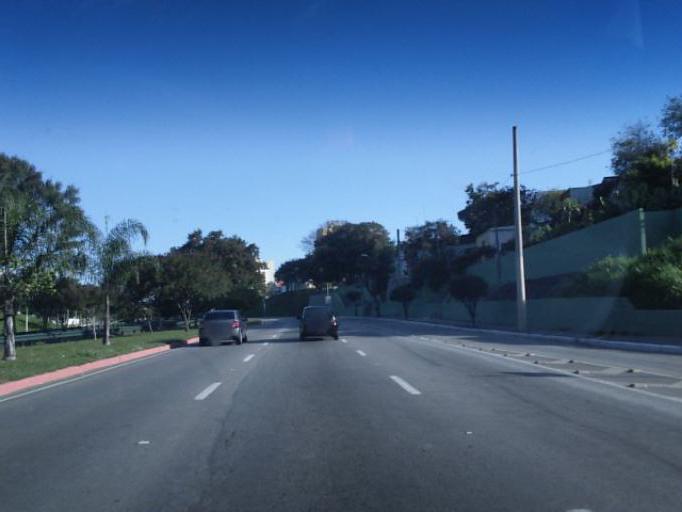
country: BR
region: Sao Paulo
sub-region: Sao Jose Dos Campos
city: Sao Jose dos Campos
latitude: -23.1914
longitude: -45.8832
